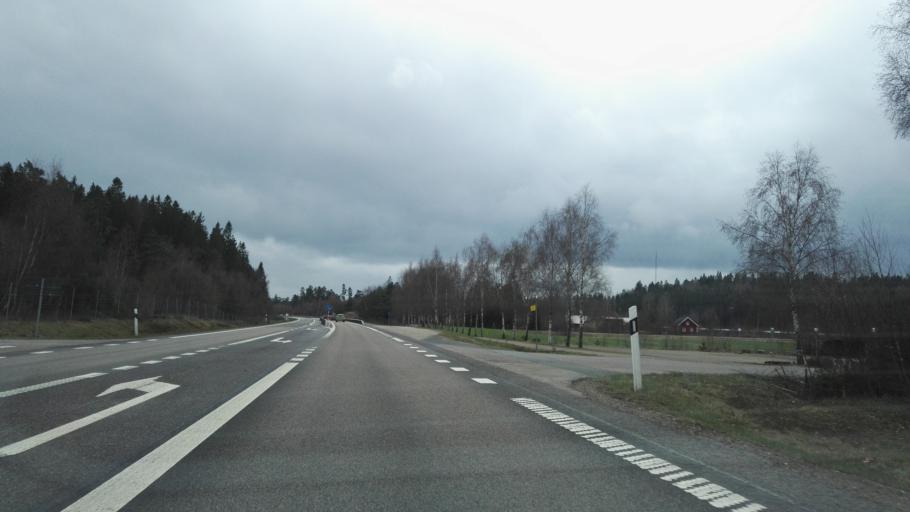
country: SE
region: Skane
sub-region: Osby Kommun
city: Osby
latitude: 56.4040
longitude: 14.0403
